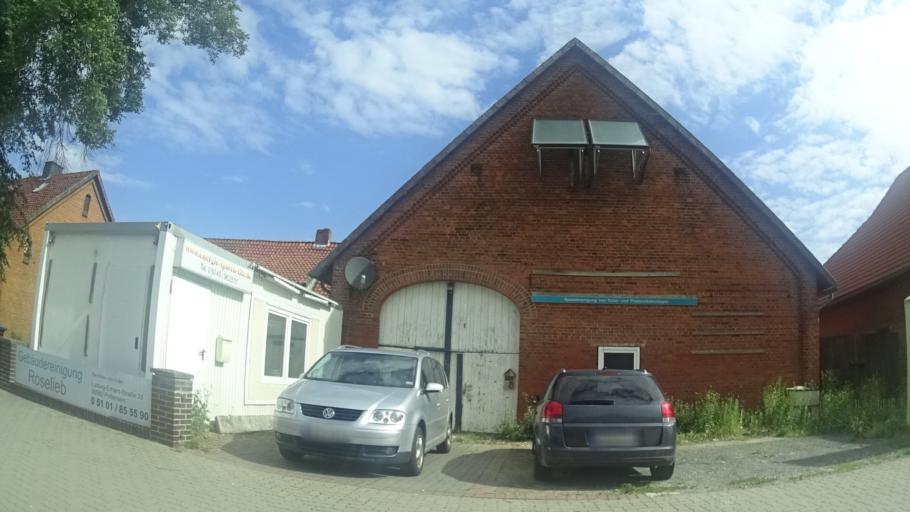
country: DE
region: Lower Saxony
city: Pattensen
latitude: 52.2123
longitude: 9.7043
